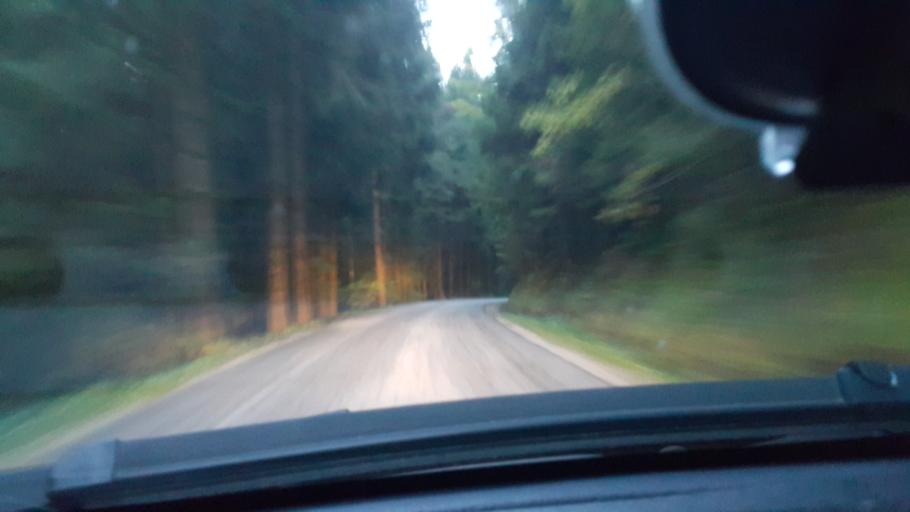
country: SI
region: Vitanje
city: Vitanje
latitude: 46.4183
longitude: 15.2759
